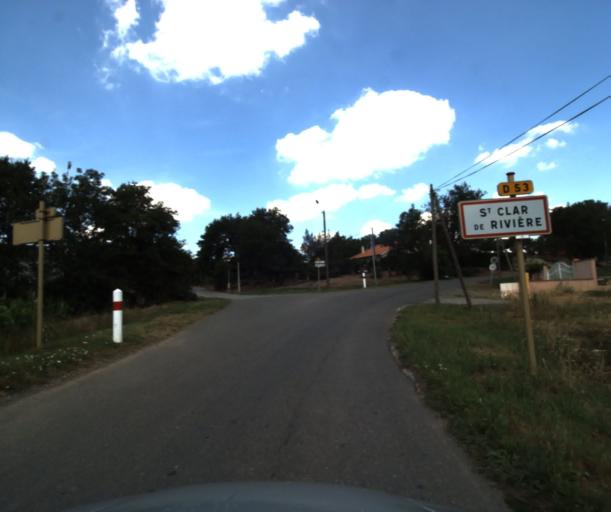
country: FR
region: Midi-Pyrenees
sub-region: Departement de la Haute-Garonne
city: Labastidette
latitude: 43.4616
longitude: 1.2171
